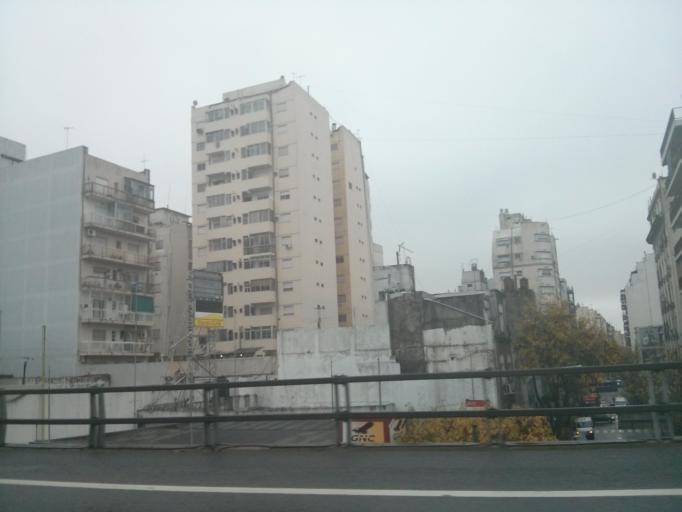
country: AR
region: Buenos Aires F.D.
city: Buenos Aires
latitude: -34.6237
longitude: -58.3928
